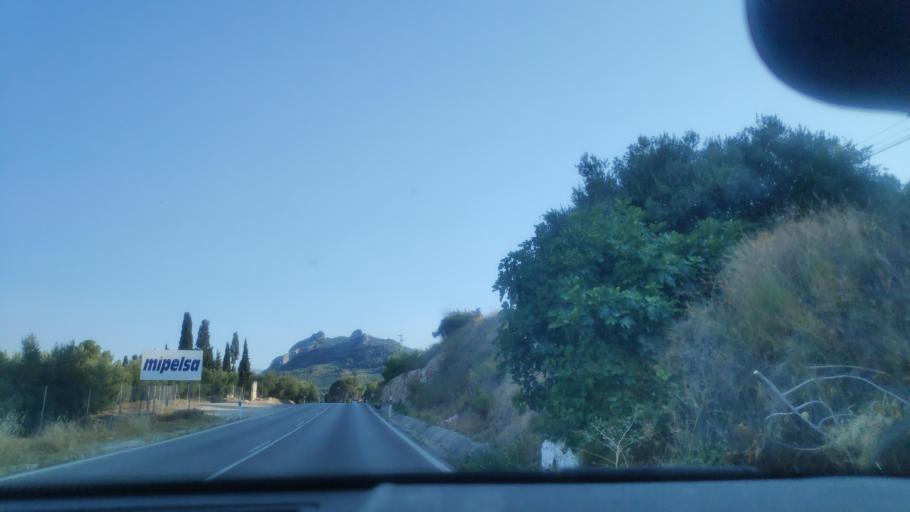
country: ES
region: Andalusia
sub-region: Provincia de Jaen
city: Jaen
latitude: 37.7580
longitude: -3.7903
